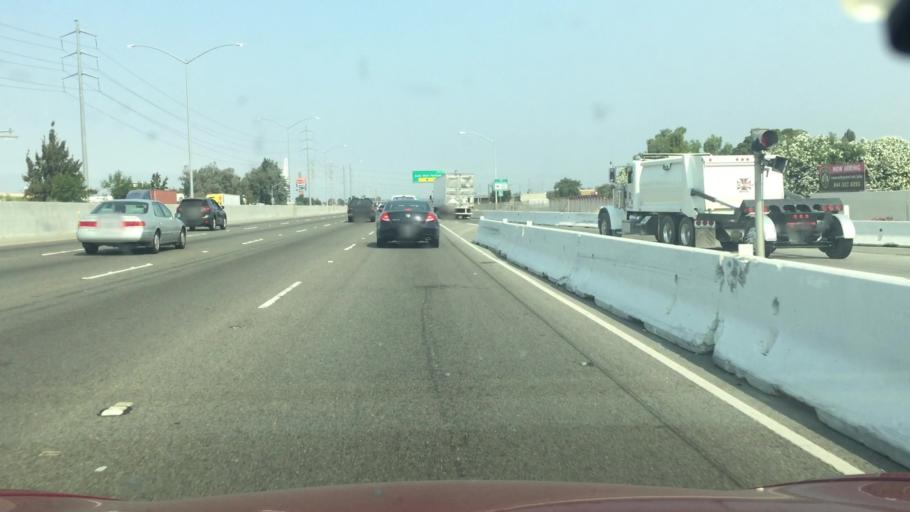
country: US
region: California
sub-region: Alameda County
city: Fremont
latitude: 37.5014
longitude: -121.9583
